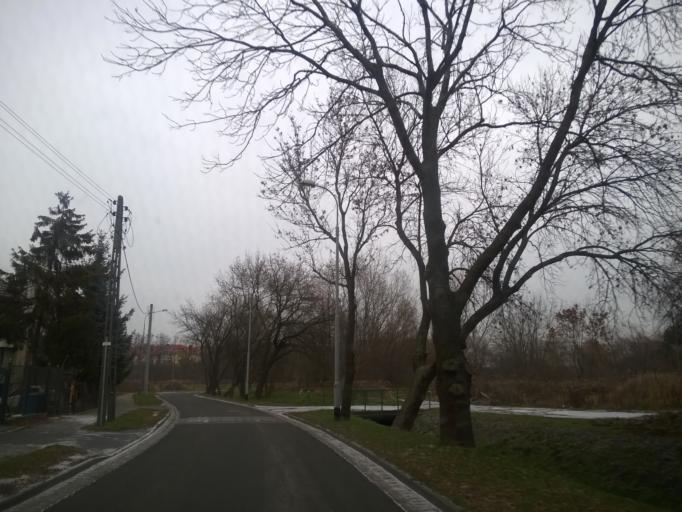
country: PL
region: Lower Silesian Voivodeship
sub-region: Powiat wroclawski
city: Wroclaw
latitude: 51.0696
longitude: 17.0434
